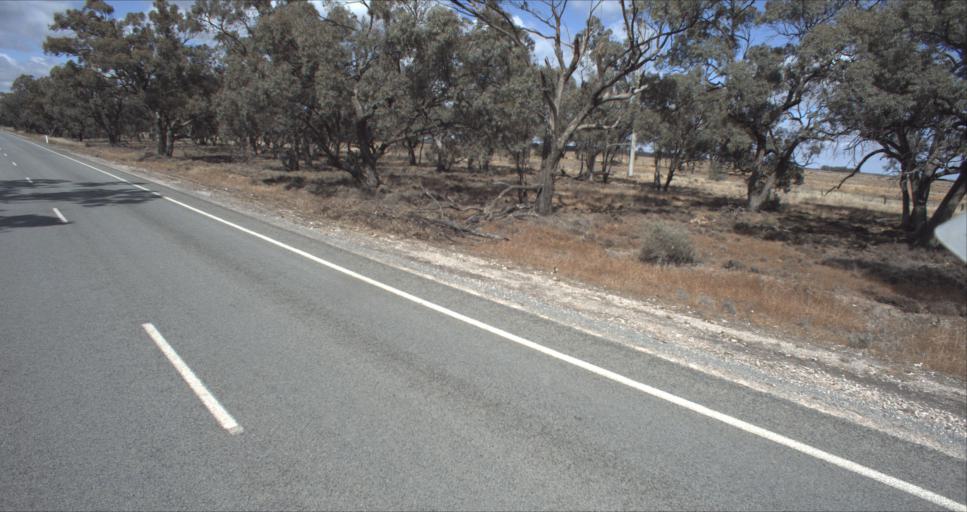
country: AU
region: New South Wales
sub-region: Murrumbidgee Shire
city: Darlington Point
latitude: -34.5646
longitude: 146.1684
